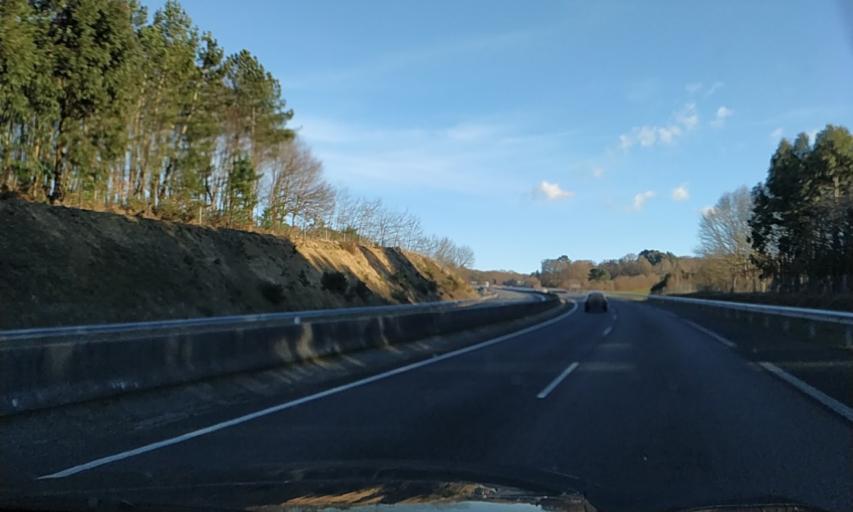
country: ES
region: Galicia
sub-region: Provincia de Pontevedra
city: Lalin
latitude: 42.6633
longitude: -8.1465
